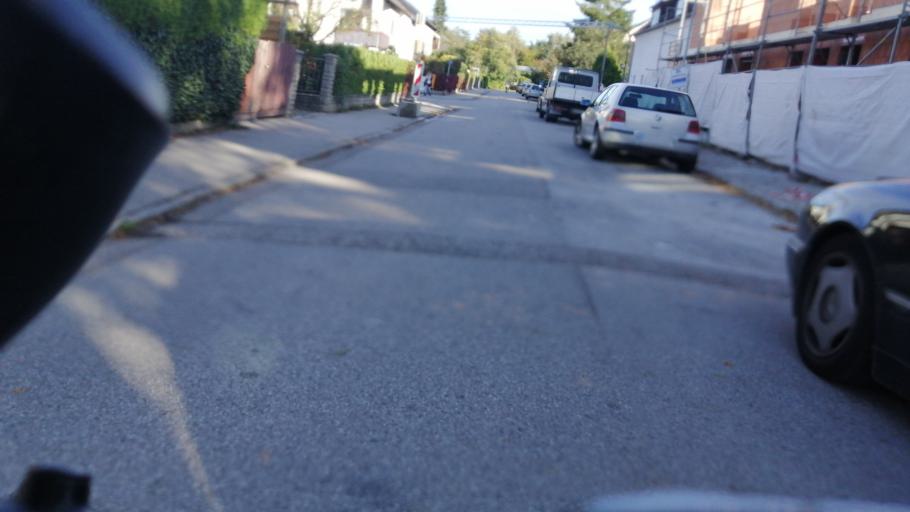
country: DE
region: Bavaria
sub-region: Upper Bavaria
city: Unterfoehring
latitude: 48.2044
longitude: 11.6108
